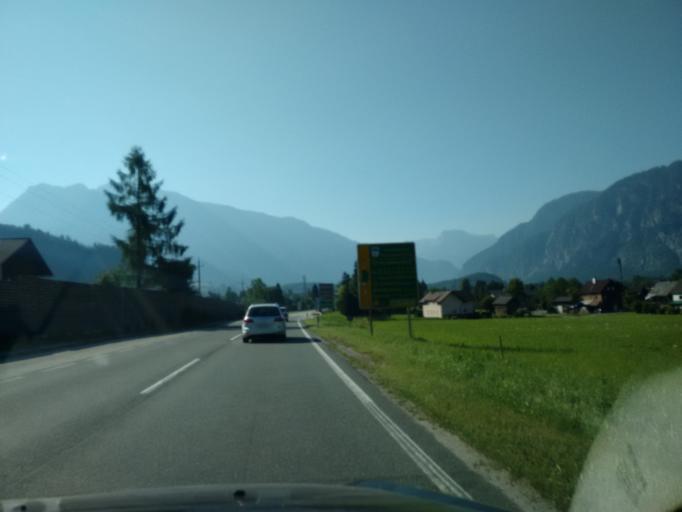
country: AT
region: Upper Austria
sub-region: Politischer Bezirk Gmunden
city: Bad Goisern
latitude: 47.6347
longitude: 13.6273
